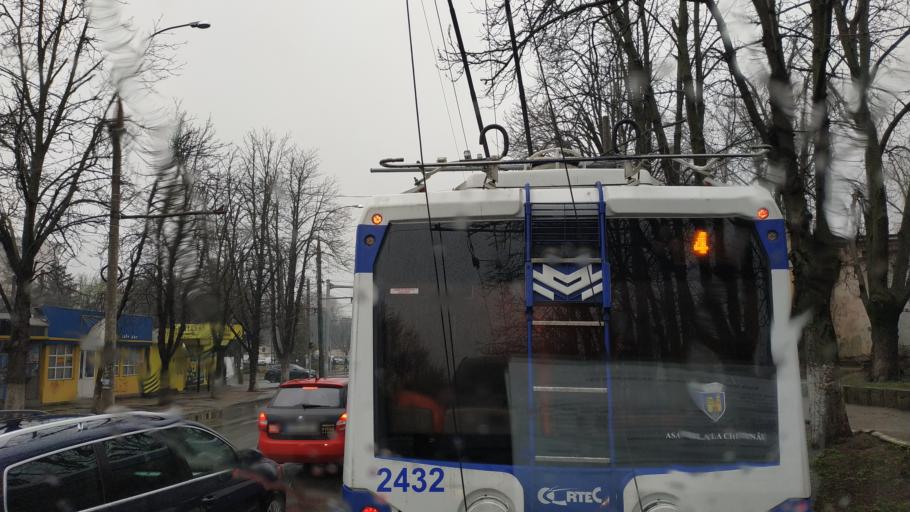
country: MD
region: Chisinau
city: Chisinau
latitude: 47.0224
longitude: 28.8037
